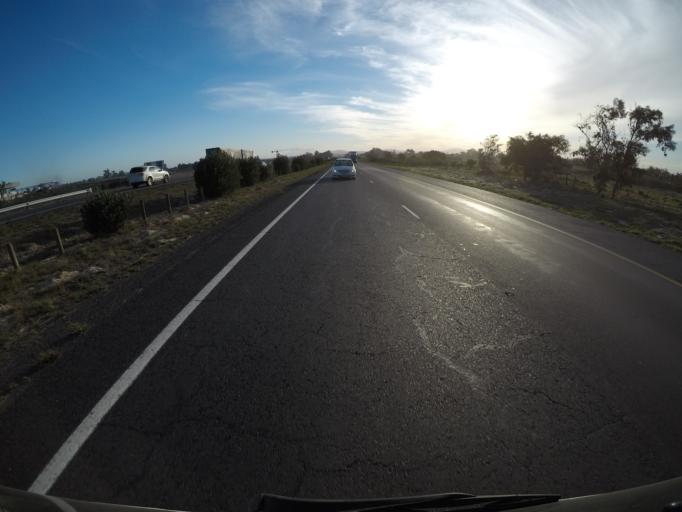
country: ZA
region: Western Cape
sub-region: City of Cape Town
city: Kraaifontein
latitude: -33.8321
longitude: 18.7472
